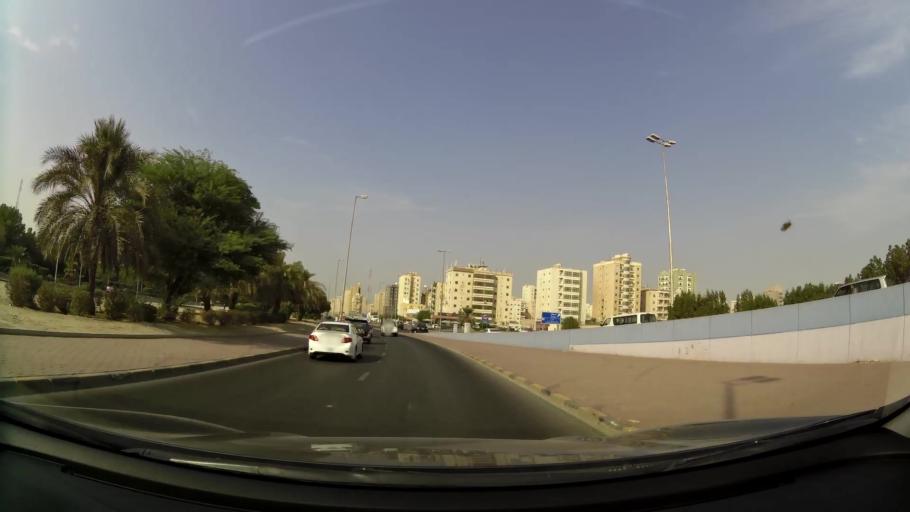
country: KW
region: Al Farwaniyah
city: Al Farwaniyah
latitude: 29.2808
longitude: 47.9683
